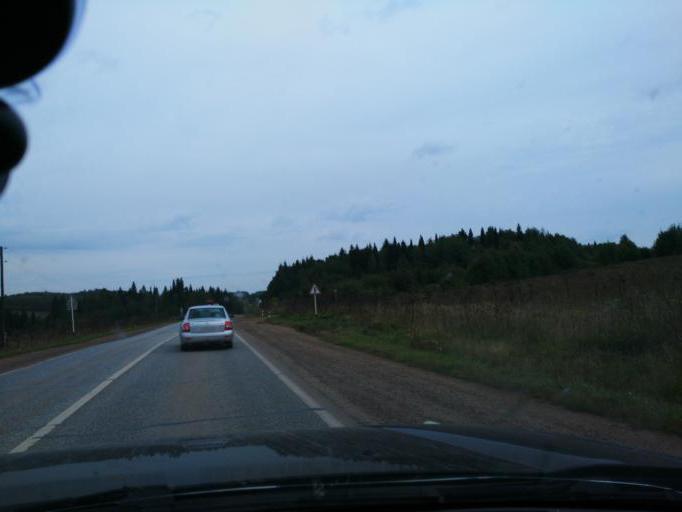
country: RU
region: Perm
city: Chernushka
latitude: 56.5666
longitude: 56.1199
